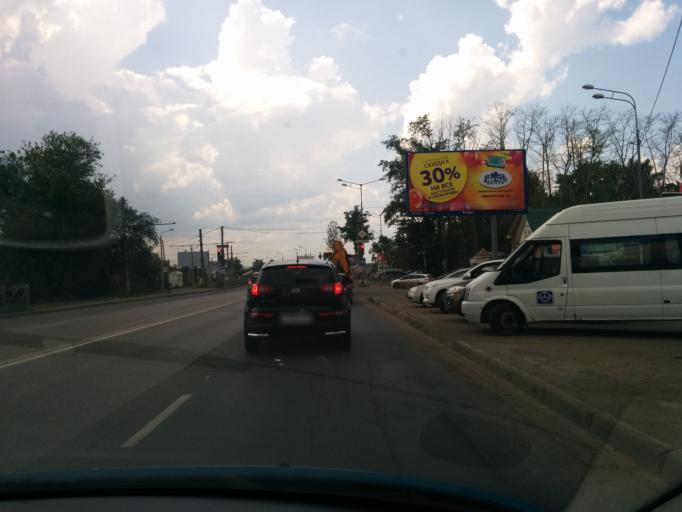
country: RU
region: Perm
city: Kondratovo
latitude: 57.9644
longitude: 56.1406
